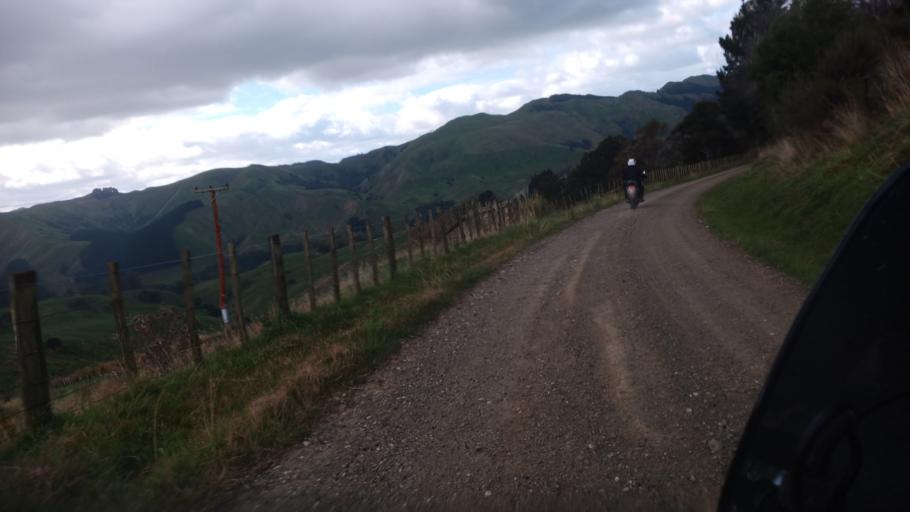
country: NZ
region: Gisborne
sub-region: Gisborne District
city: Gisborne
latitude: -38.4643
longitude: 177.6251
